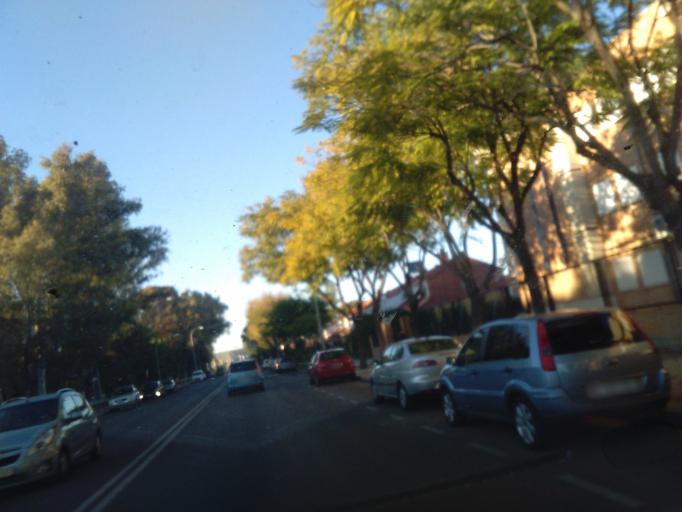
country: ES
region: Andalusia
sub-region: Provincia de Sevilla
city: Sevilla
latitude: 37.3982
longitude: -5.9308
